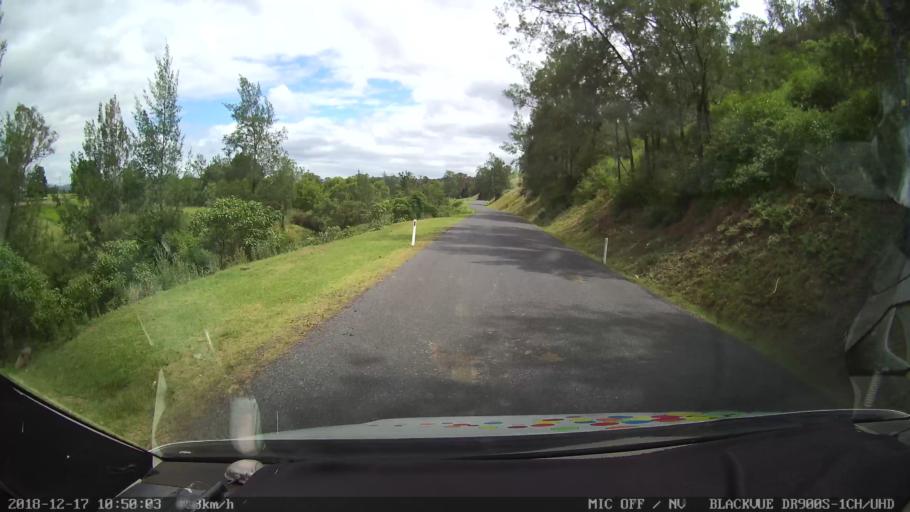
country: AU
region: New South Wales
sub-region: Clarence Valley
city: Gordon
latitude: -28.8627
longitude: 152.5742
